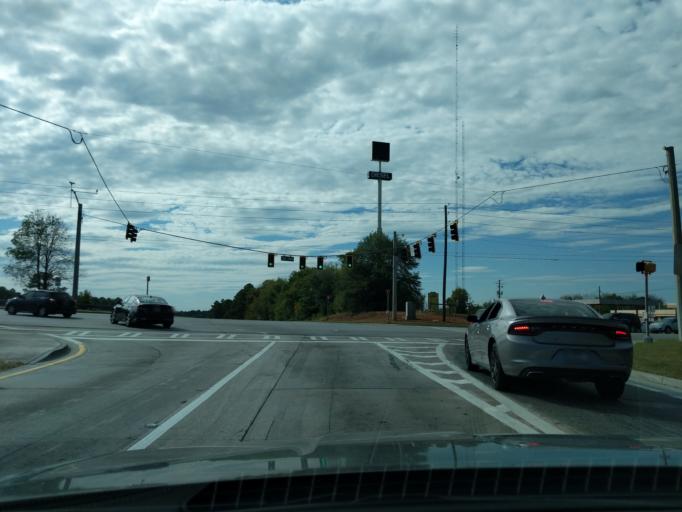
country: US
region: Georgia
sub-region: Columbia County
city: Grovetown
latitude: 33.4846
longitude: -82.1991
